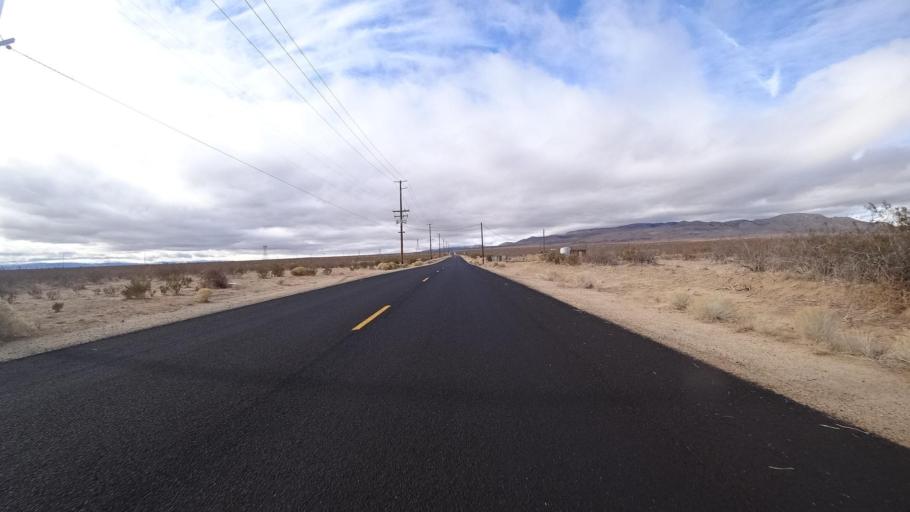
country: US
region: California
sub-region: Kern County
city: Mojave
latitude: 34.9510
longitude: -118.3034
